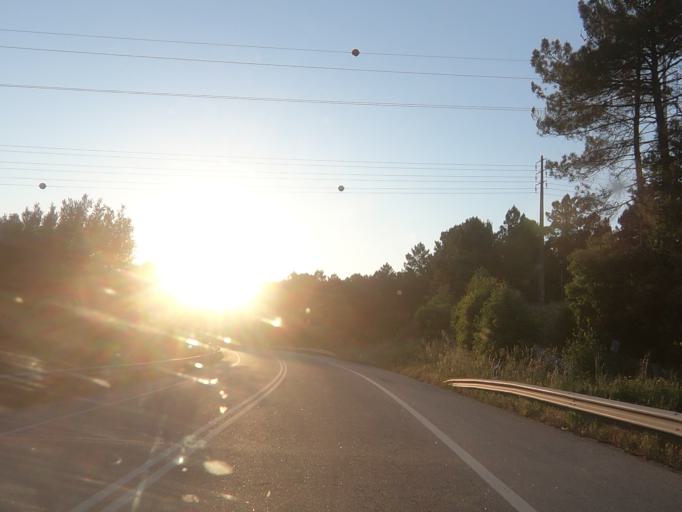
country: PT
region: Viseu
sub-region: Viseu
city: Rio de Loba
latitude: 40.6736
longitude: -7.8618
